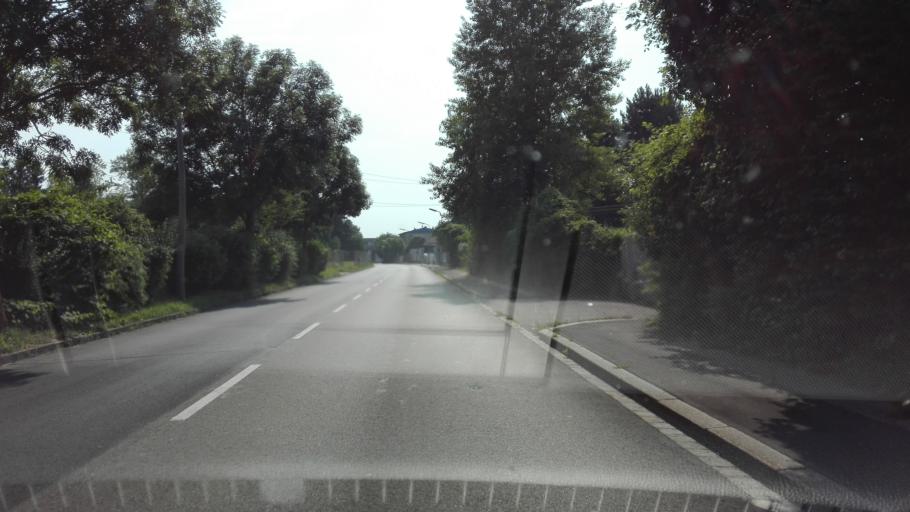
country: AT
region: Upper Austria
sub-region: Politischer Bezirk Linz-Land
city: Ansfelden
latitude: 48.2371
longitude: 14.2814
